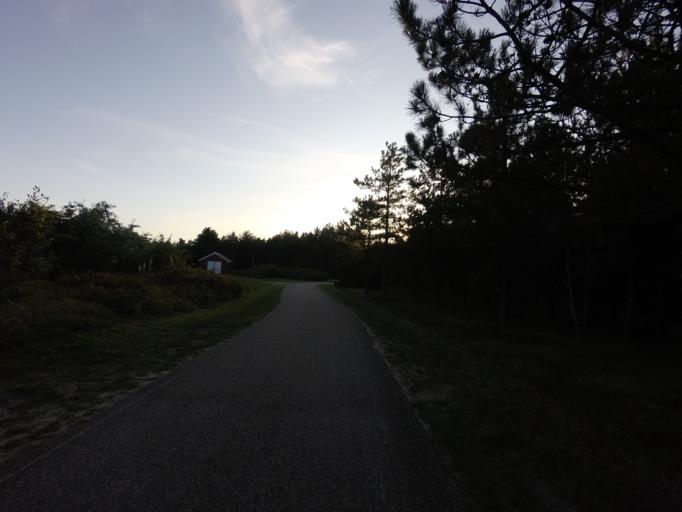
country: NL
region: Friesland
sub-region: Gemeente Ameland
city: Nes
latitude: 53.4523
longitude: 5.7804
